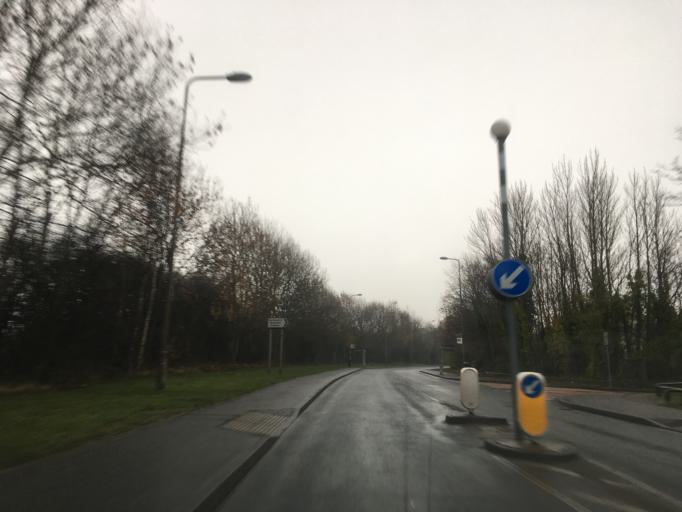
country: GB
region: Scotland
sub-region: Edinburgh
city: Colinton
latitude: 55.9148
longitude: -3.2772
